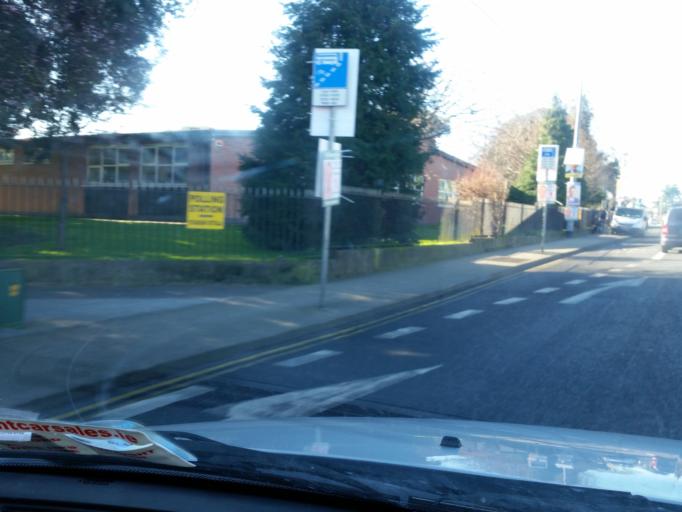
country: IE
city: Killester
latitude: 53.3754
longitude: -6.1950
